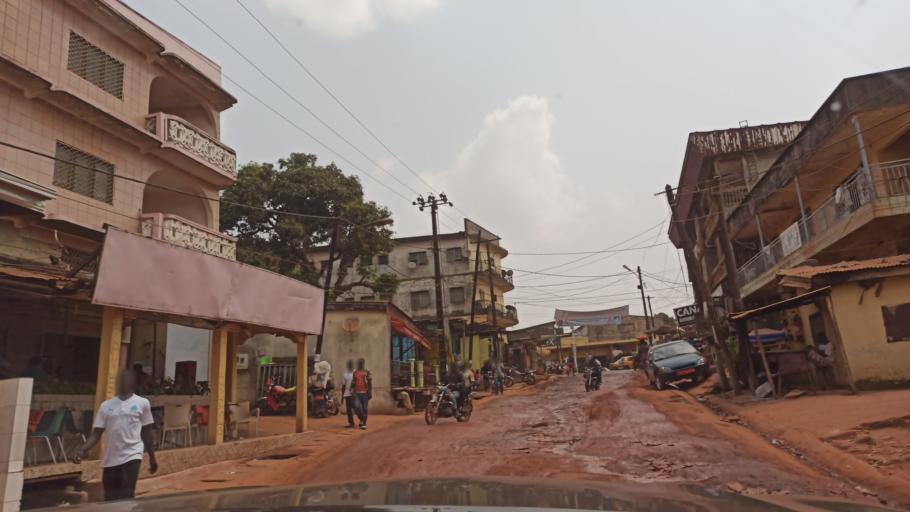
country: CM
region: Centre
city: Yaounde
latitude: 3.8852
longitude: 11.4914
